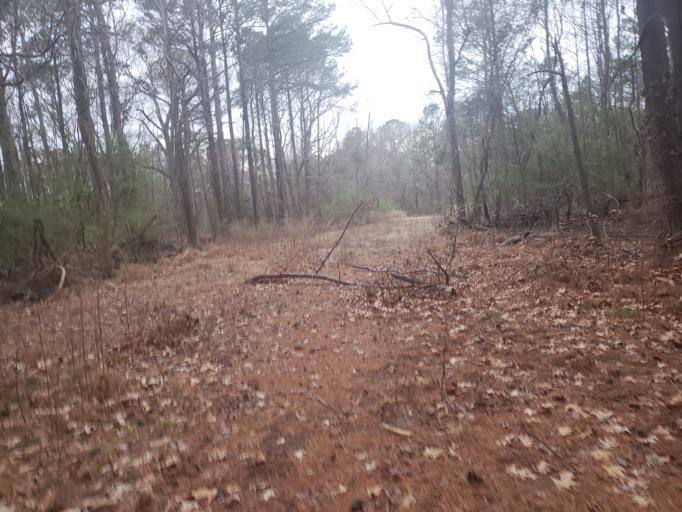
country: US
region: Virginia
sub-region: City of Newport News
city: Newport News
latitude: 36.8967
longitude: -76.4308
